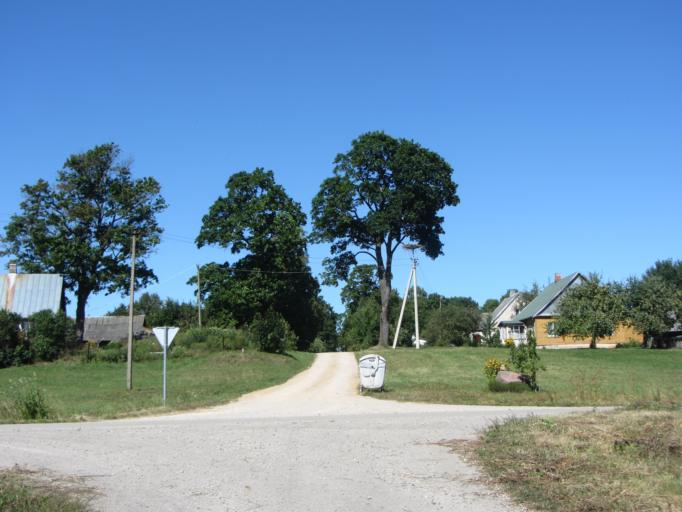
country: LT
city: Kupiskis
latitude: 55.8431
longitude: 25.0605
